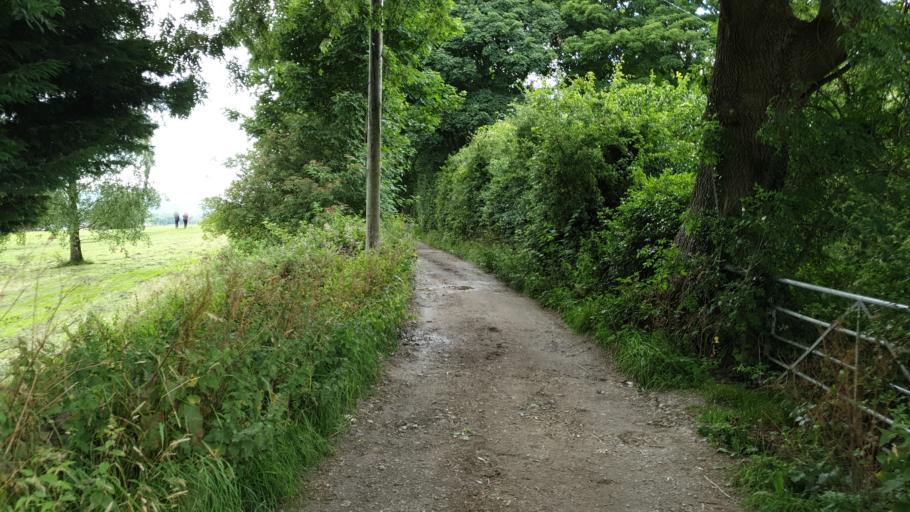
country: GB
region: England
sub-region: City and Borough of Leeds
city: Guiseley
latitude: 53.8799
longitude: -1.7129
